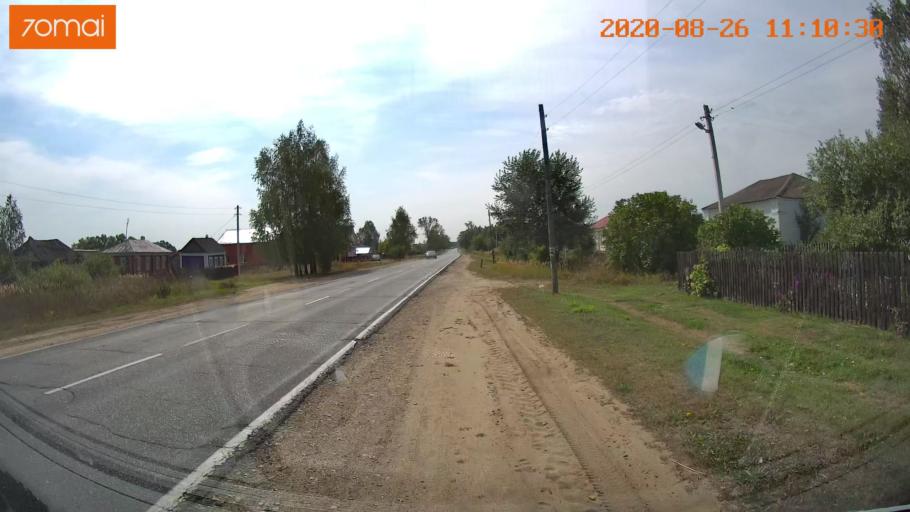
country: RU
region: Rjazan
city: Izhevskoye
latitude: 54.4778
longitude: 41.1261
